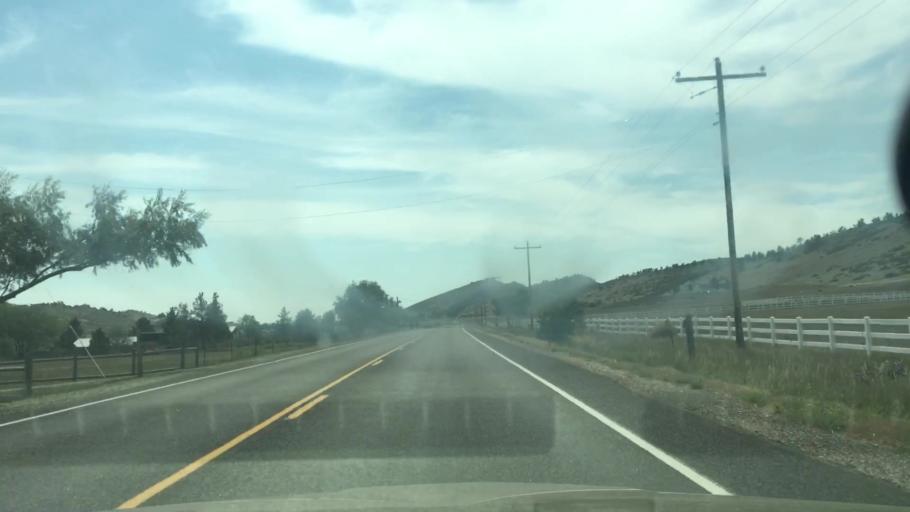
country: US
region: Colorado
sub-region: Larimer County
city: Campion
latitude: 40.3800
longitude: -105.1976
